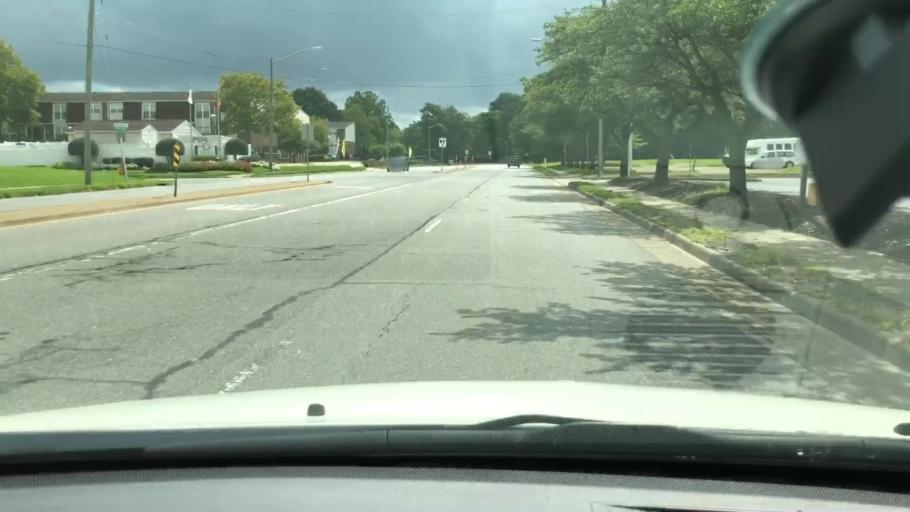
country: US
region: Virginia
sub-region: City of Chesapeake
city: Chesapeake
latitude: 36.8112
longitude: -76.2147
